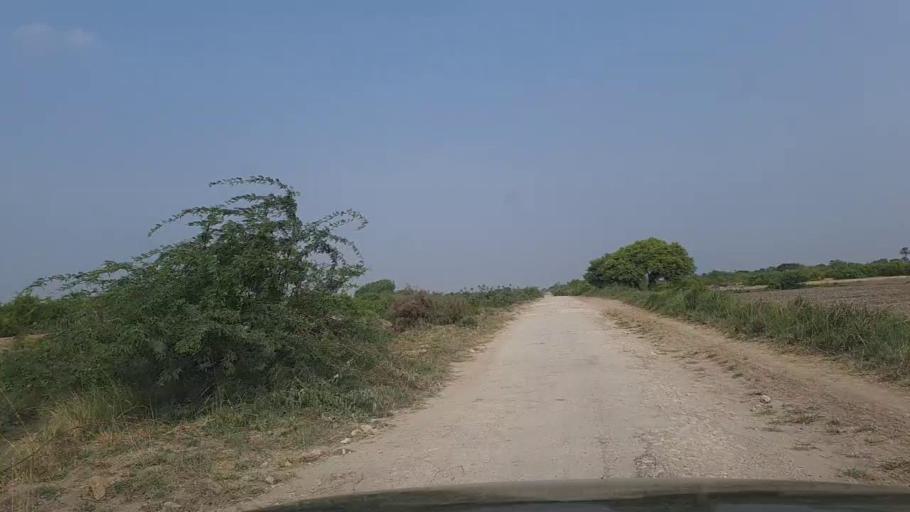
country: PK
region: Sindh
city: Thatta
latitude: 24.7497
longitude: 67.8080
